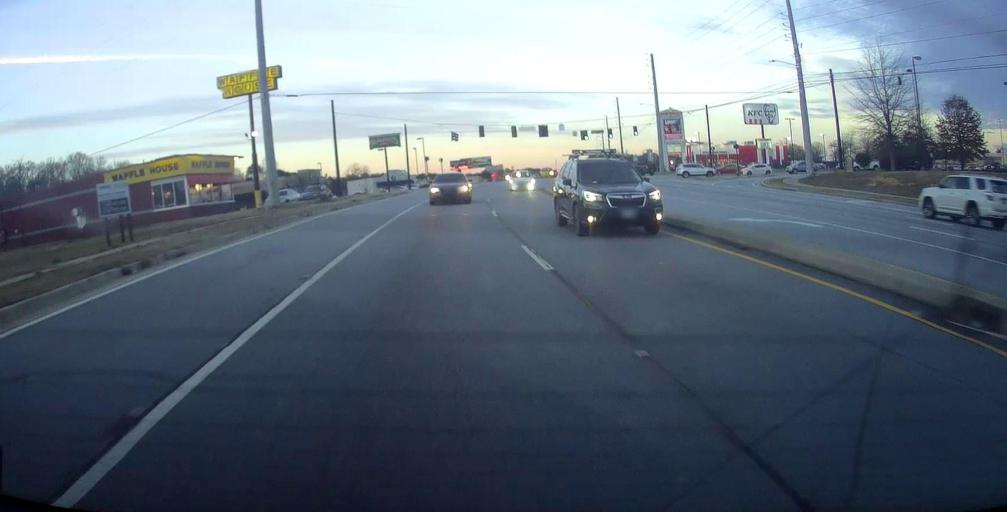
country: US
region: Alabama
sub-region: Russell County
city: Phenix City
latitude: 32.5420
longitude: -84.9547
